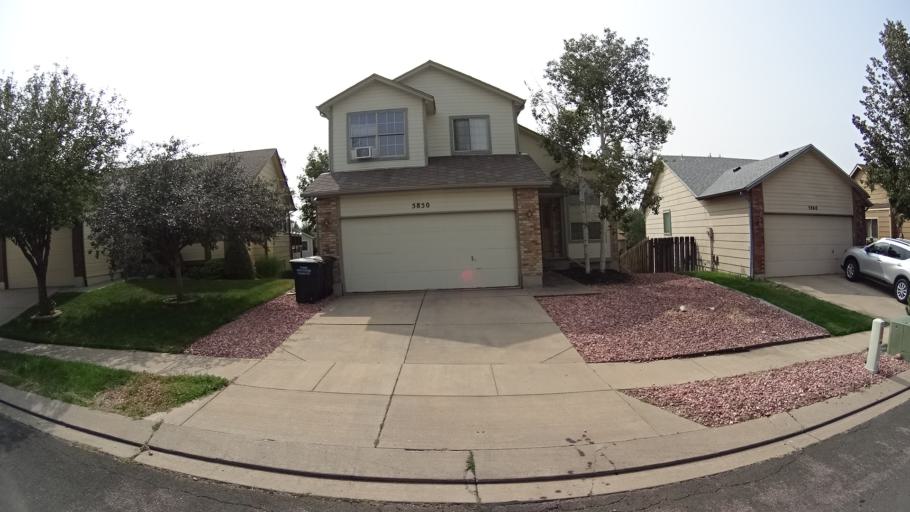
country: US
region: Colorado
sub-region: El Paso County
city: Cimarron Hills
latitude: 38.9194
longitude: -104.7314
